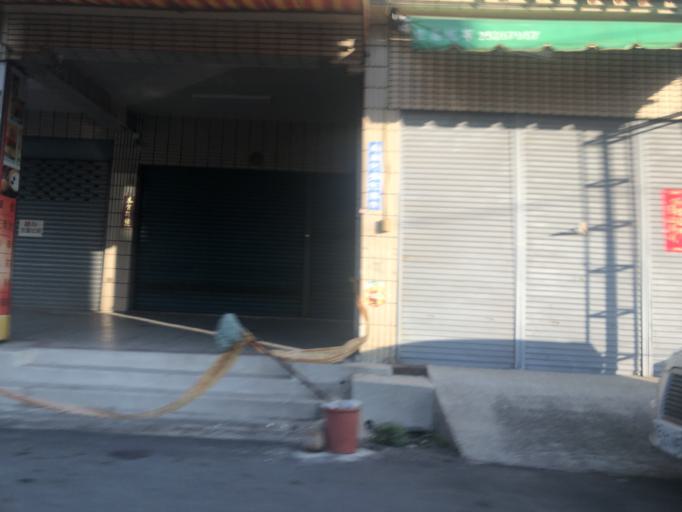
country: TW
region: Taiwan
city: Fengyuan
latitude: 24.2551
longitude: 120.7257
